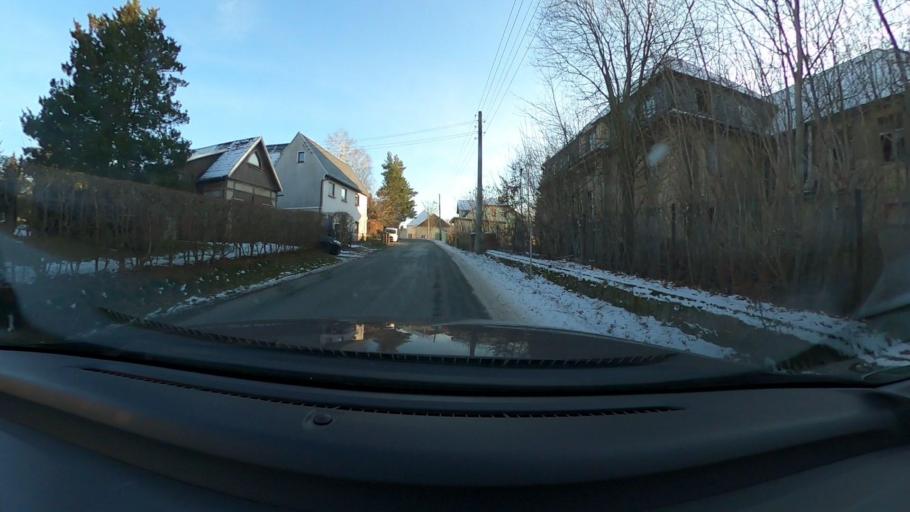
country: DE
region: Saxony
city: Frankenstein
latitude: 50.9390
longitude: 13.2202
